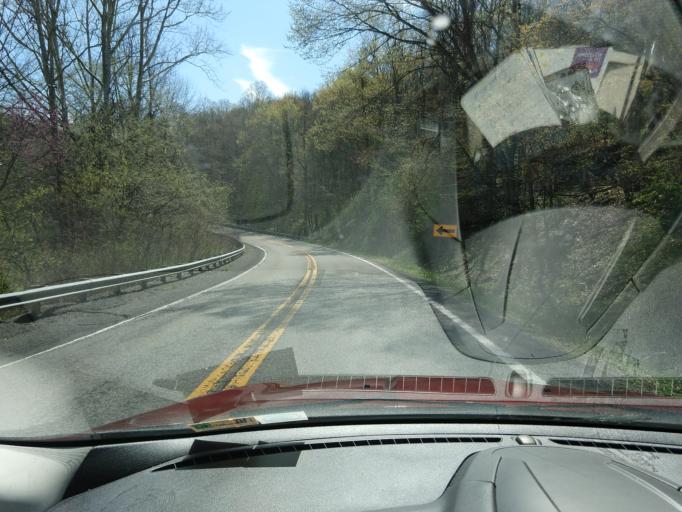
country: US
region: West Virginia
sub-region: Greenbrier County
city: Ronceverte
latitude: 37.7565
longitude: -80.5332
